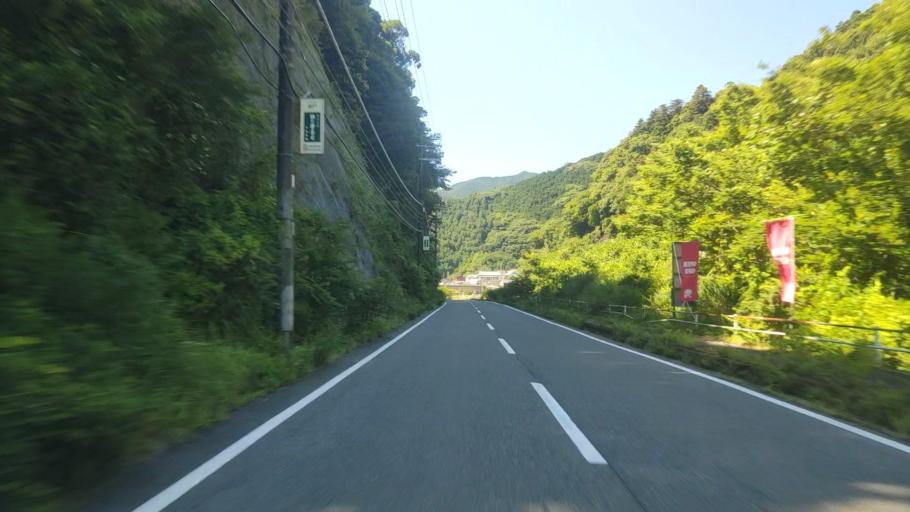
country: JP
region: Nara
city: Yoshino-cho
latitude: 34.2985
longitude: 136.0001
